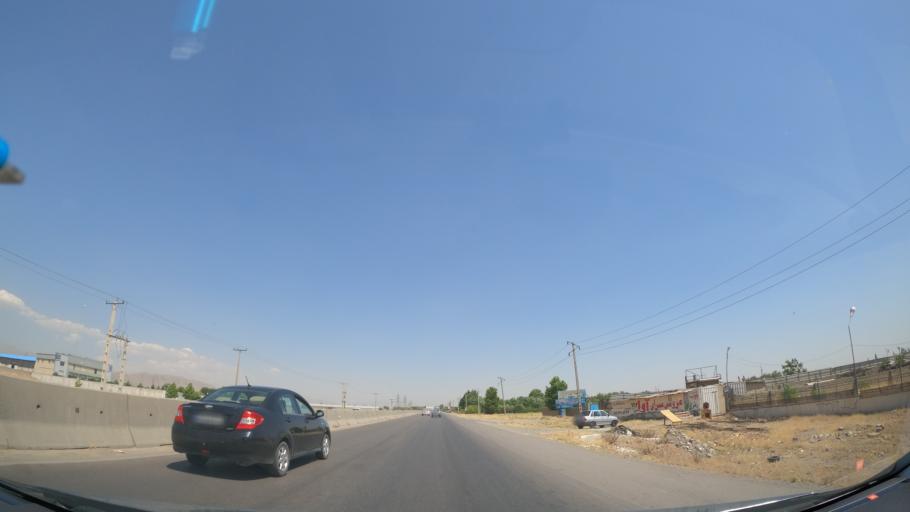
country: IR
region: Alborz
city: Hashtgerd
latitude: 35.9273
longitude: 50.7339
